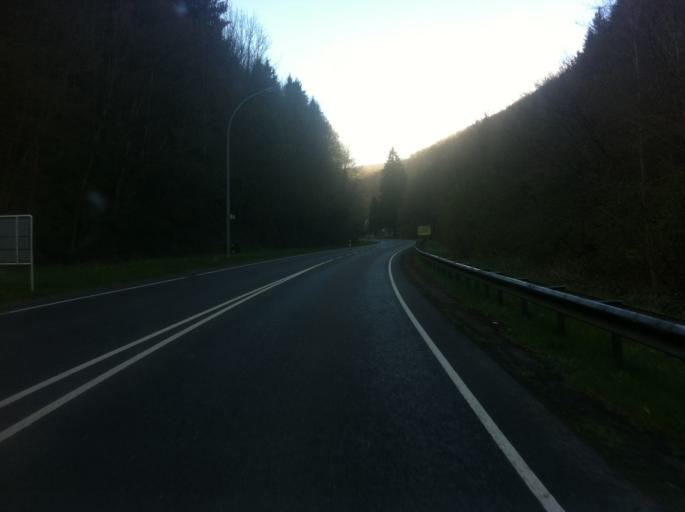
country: LU
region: Diekirch
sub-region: Canton de Wiltz
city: Esch-sur-Sure
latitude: 49.9101
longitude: 5.9500
